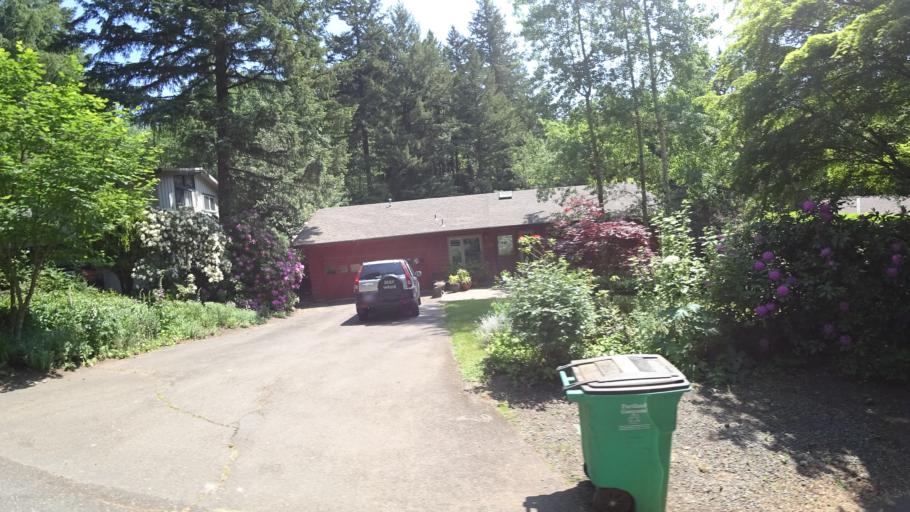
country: US
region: Oregon
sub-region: Washington County
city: West Slope
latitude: 45.5144
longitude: -122.7248
